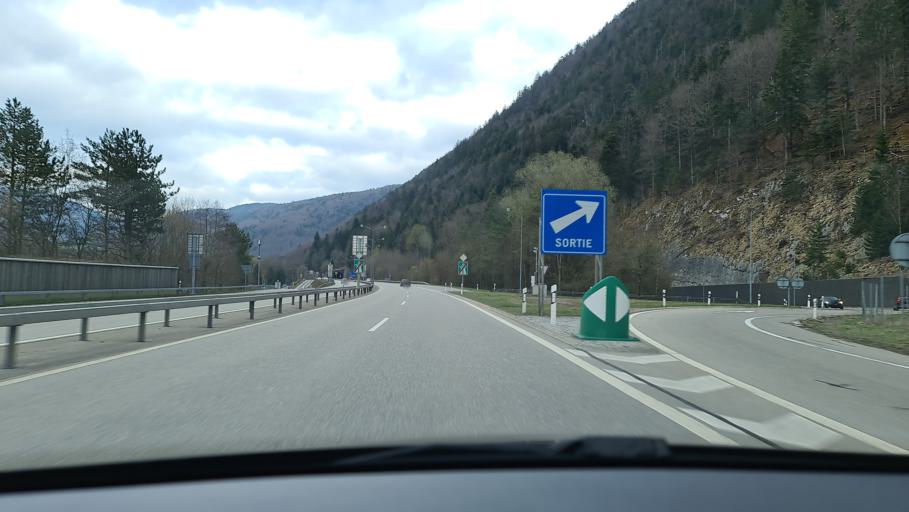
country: CH
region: Bern
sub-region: Jura bernois
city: Pery
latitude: 47.1872
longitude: 7.2286
